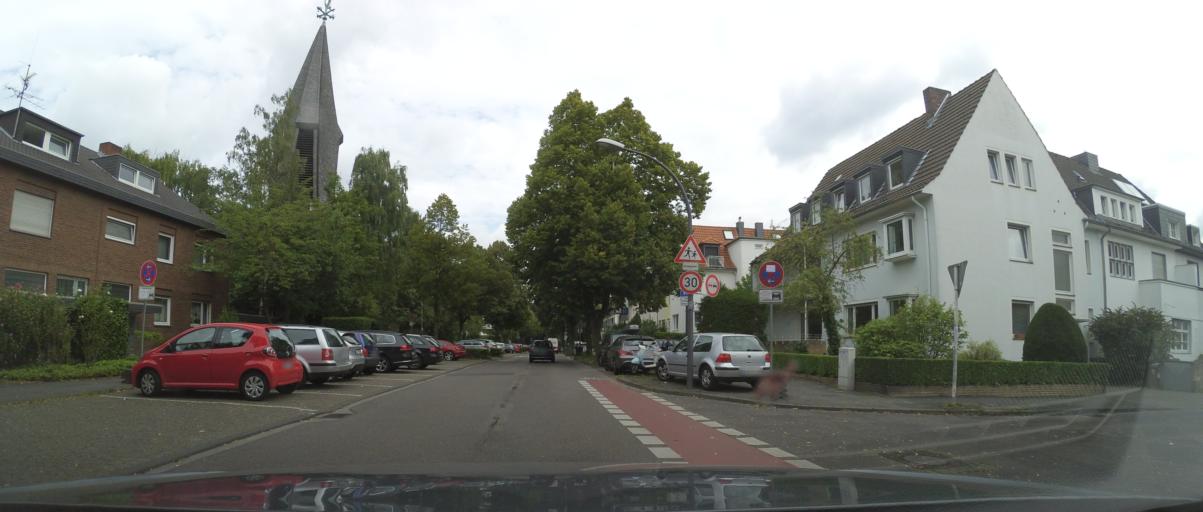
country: DE
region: North Rhine-Westphalia
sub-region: Regierungsbezirk Koln
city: Neustadt/Sued
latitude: 50.9248
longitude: 6.9002
